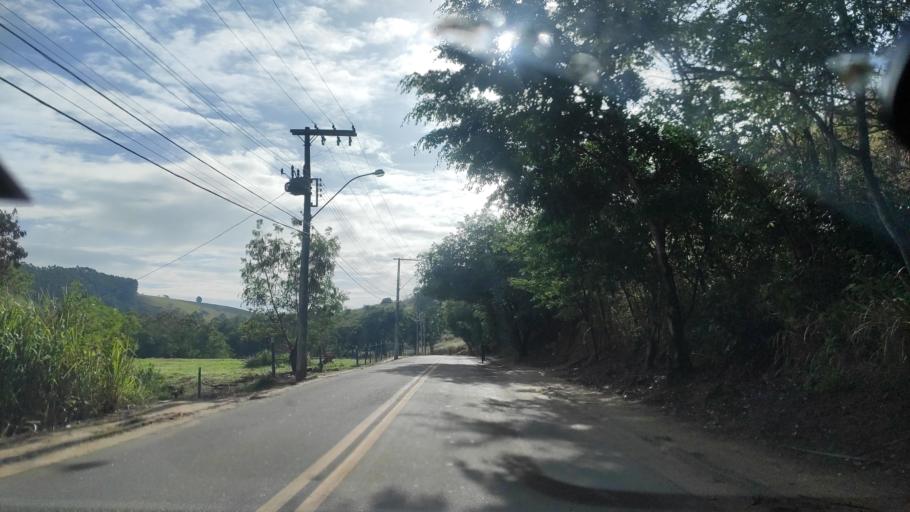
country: BR
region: Espirito Santo
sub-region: Nova Venecia
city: Nova Venecia
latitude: -18.7165
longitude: -40.3872
